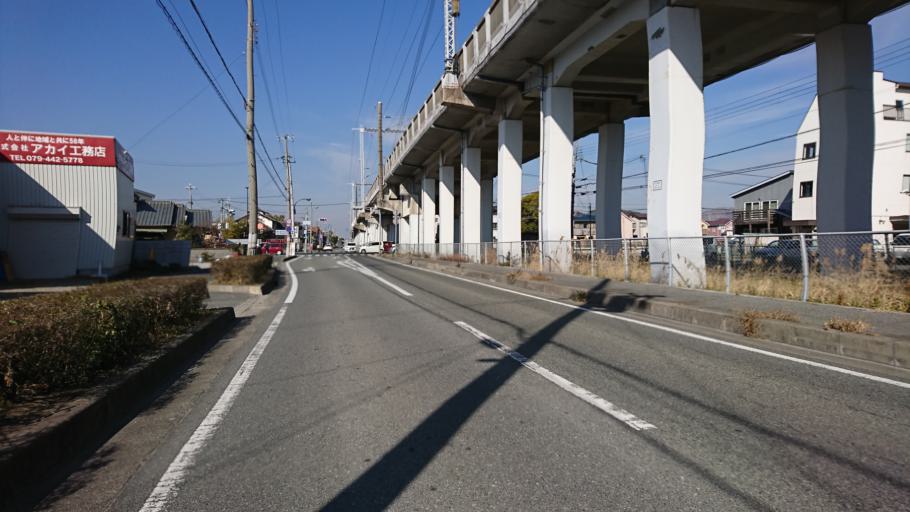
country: JP
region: Hyogo
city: Kakogawacho-honmachi
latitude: 34.7639
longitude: 134.8027
